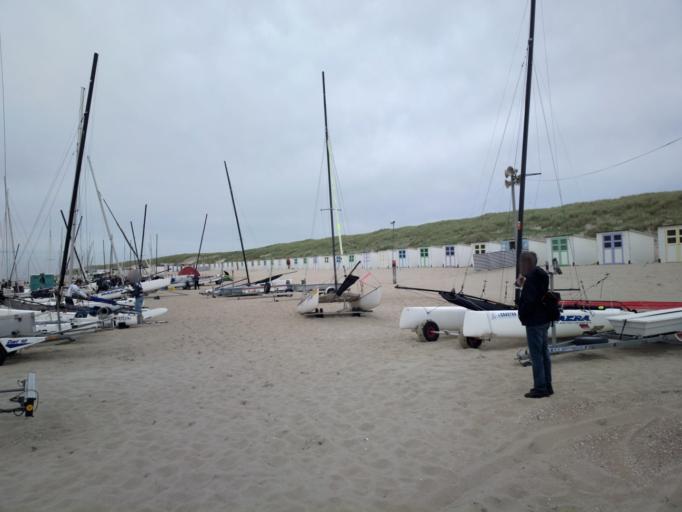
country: NL
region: North Holland
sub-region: Gemeente Texel
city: Den Burg
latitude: 53.0822
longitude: 4.7367
